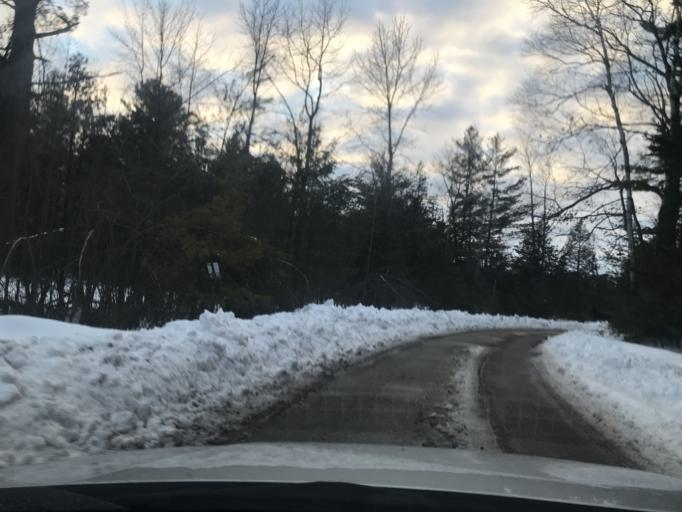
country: US
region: Wisconsin
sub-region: Marinette County
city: Marinette
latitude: 45.1147
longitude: -87.6697
